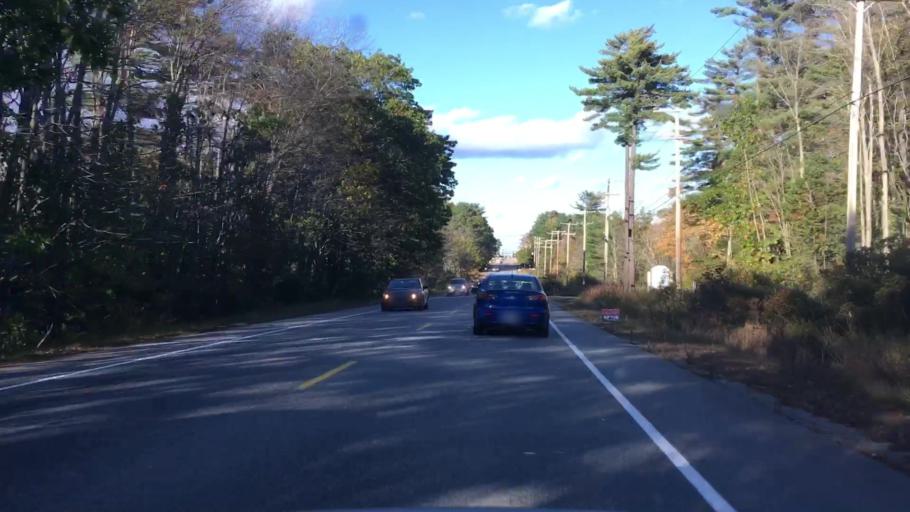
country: US
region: Maine
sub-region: Cumberland County
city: South Portland Gardens
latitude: 43.6146
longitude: -70.3564
